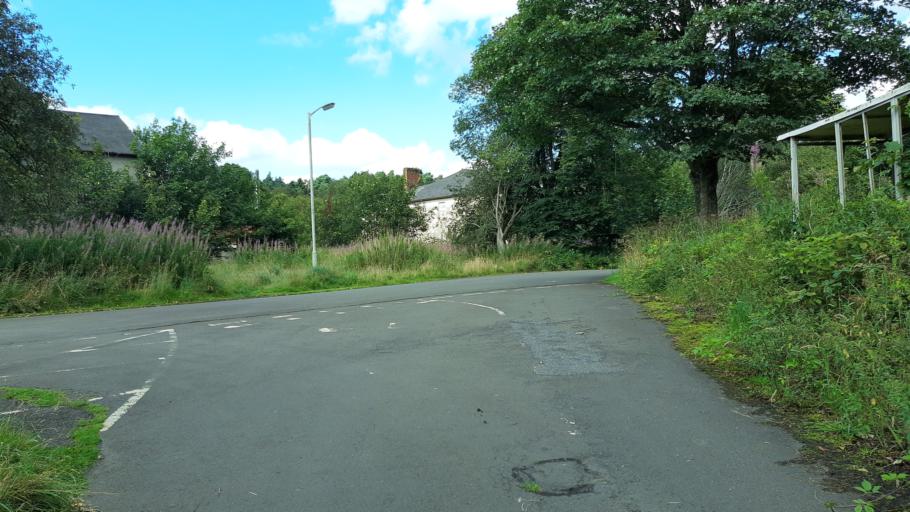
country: GB
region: Scotland
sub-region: West Lothian
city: Livingston
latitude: 55.9196
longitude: -3.5588
